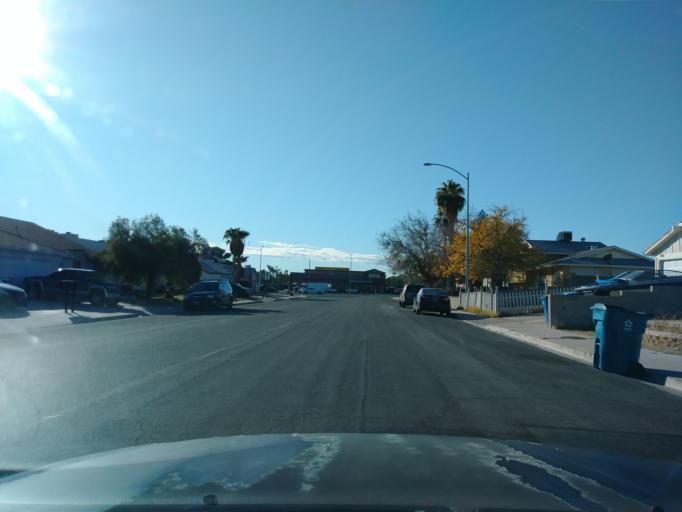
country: US
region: Nevada
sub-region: Clark County
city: Spring Valley
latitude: 36.1602
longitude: -115.2465
